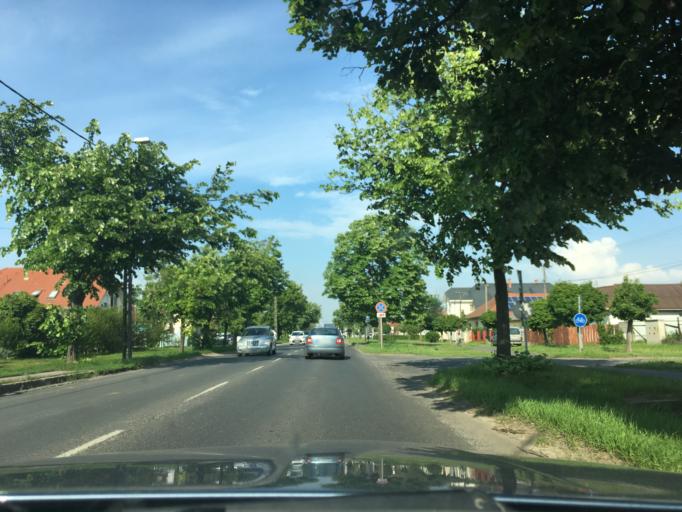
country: HU
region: Hajdu-Bihar
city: Debrecen
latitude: 47.5446
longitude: 21.6458
